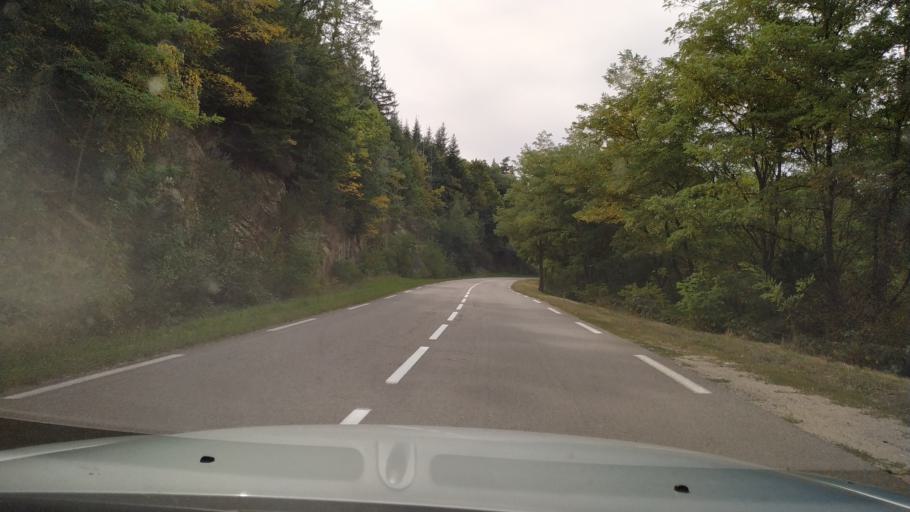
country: FR
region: Rhone-Alpes
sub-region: Departement de l'Ardeche
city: Lamastre
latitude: 44.9865
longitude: 4.5527
